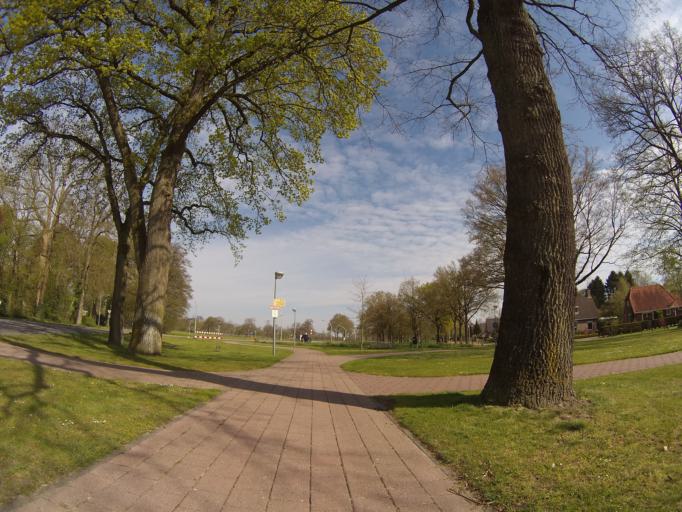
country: NL
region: Drenthe
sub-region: Gemeente Coevorden
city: Sleen
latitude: 52.7950
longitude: 6.7285
